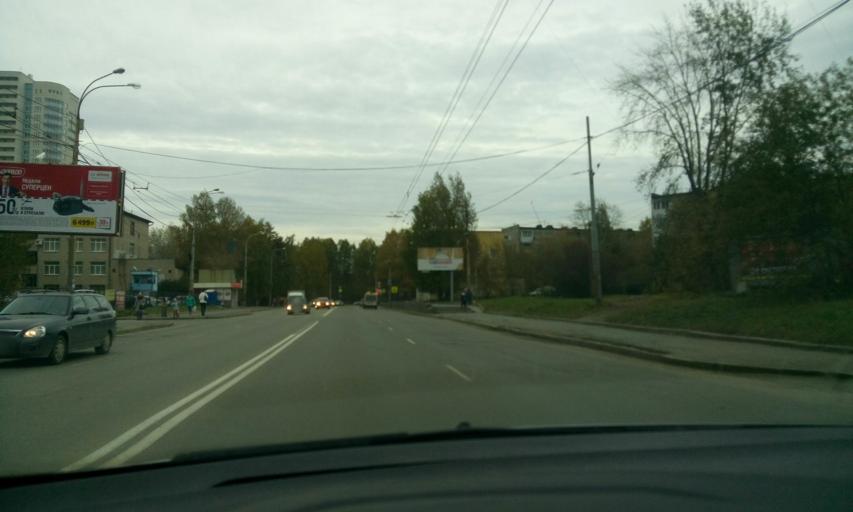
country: RU
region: Sverdlovsk
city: Yekaterinburg
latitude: 56.8609
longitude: 60.6505
